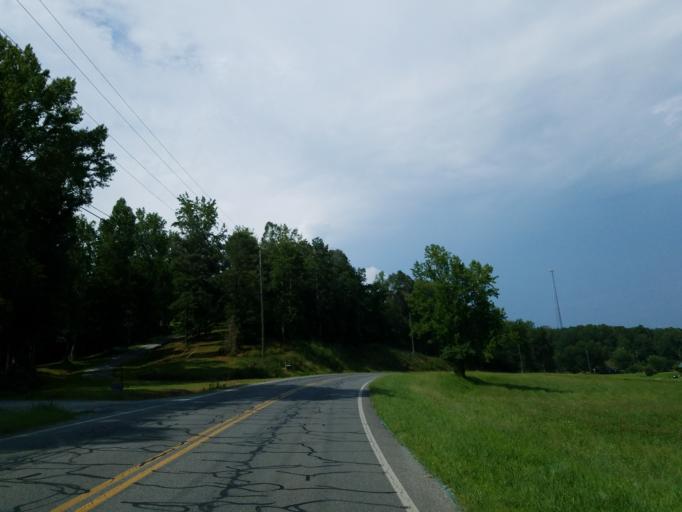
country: US
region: Georgia
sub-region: Gilmer County
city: Ellijay
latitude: 34.6139
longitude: -84.5941
